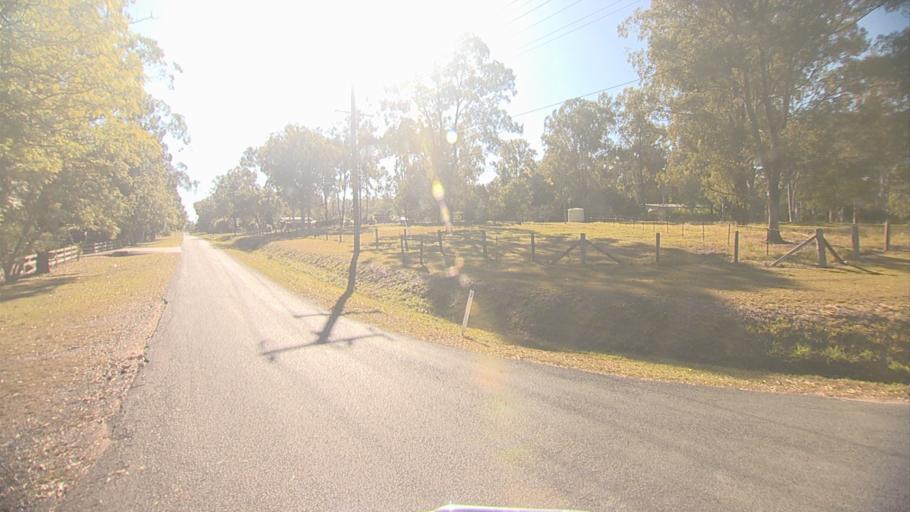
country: AU
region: Queensland
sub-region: Logan
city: Park Ridge South
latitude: -27.7560
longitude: 153.0465
